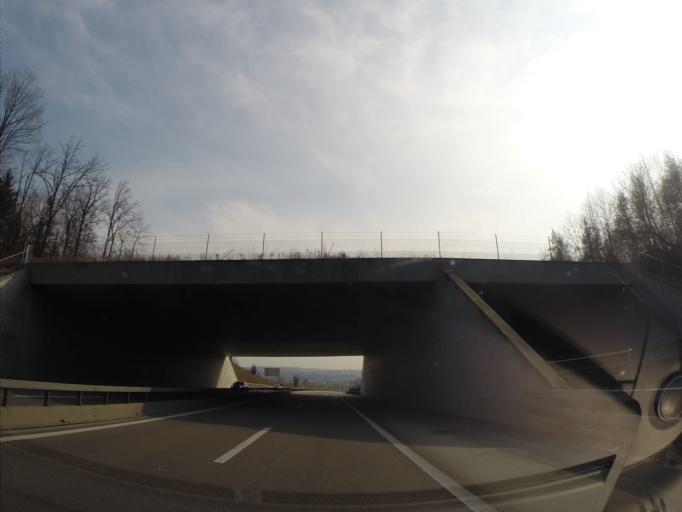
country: CH
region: Zurich
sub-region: Bezirk Andelfingen
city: Kleinandelfingen
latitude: 47.6132
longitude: 8.6858
